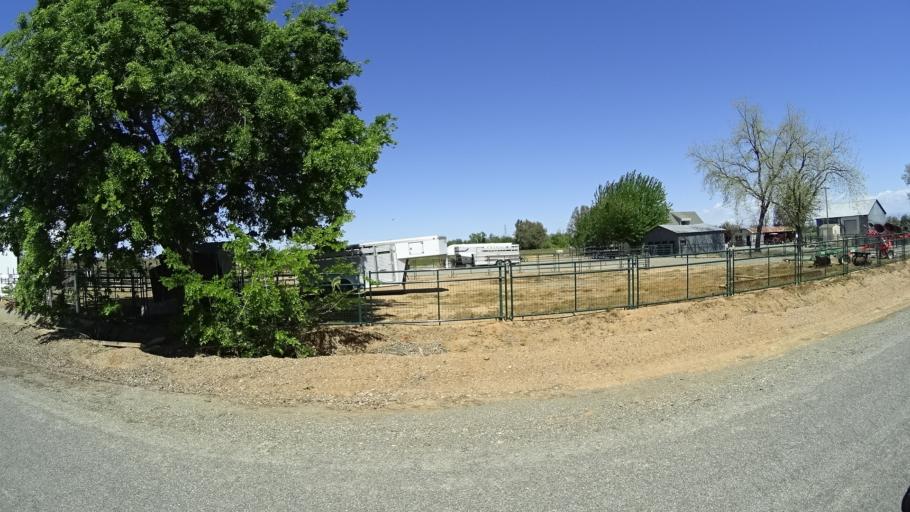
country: US
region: California
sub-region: Glenn County
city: Orland
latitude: 39.7947
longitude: -122.2091
